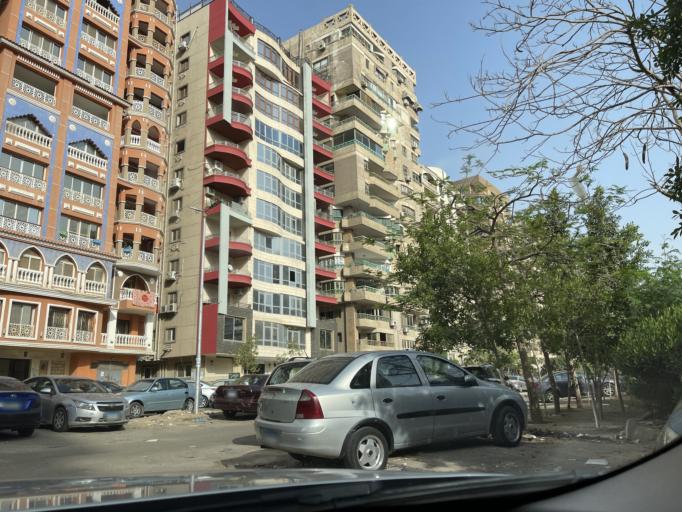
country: EG
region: Muhafazat al Qahirah
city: Cairo
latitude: 30.0676
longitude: 31.3557
